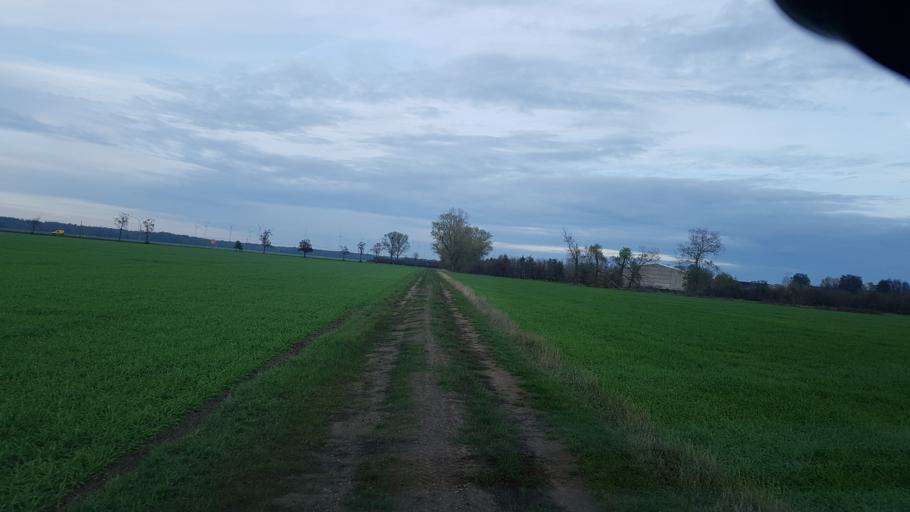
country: DE
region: Brandenburg
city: Falkenberg
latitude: 51.5403
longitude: 13.2736
